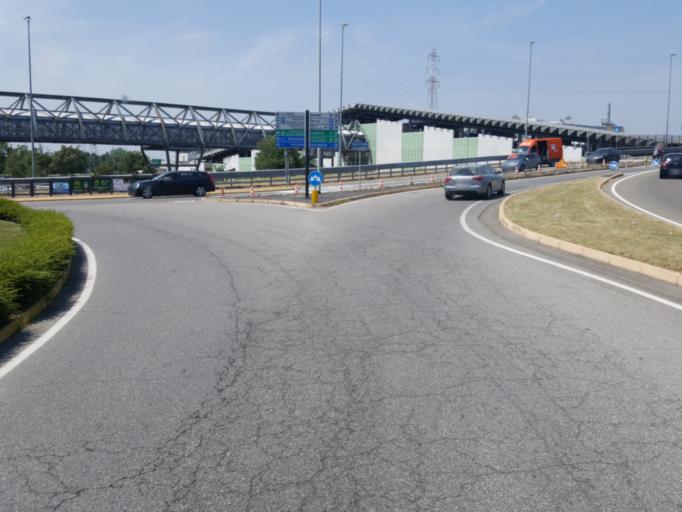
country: IT
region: Lombardy
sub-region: Citta metropolitana di Milano
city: Rozzano
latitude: 45.4023
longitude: 9.1474
